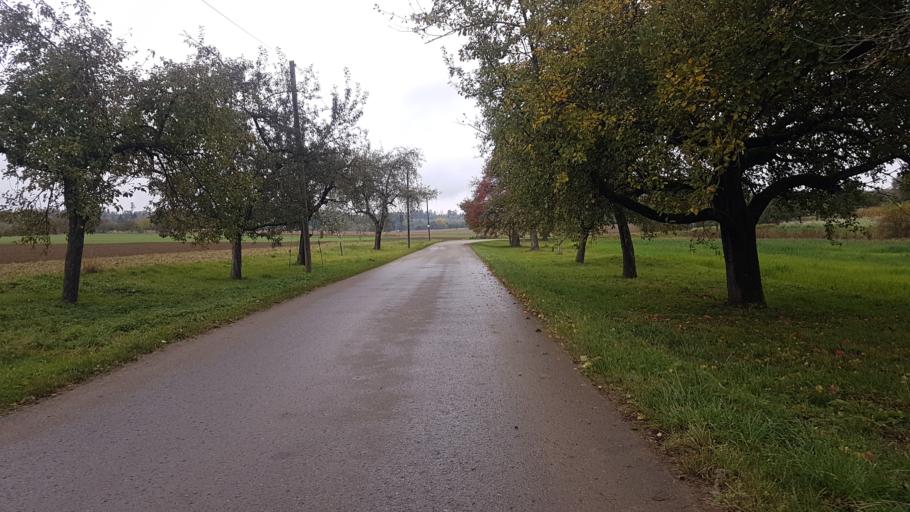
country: DE
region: Baden-Wuerttemberg
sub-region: Tuebingen Region
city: Dusslingen
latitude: 48.4467
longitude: 9.0439
